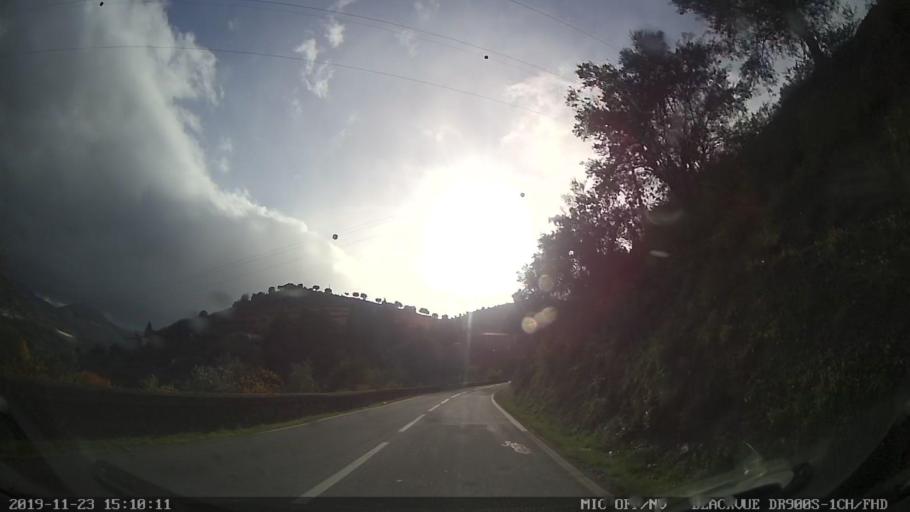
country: PT
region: Vila Real
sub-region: Peso da Regua
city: Peso da Regua
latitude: 41.1435
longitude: -7.7795
